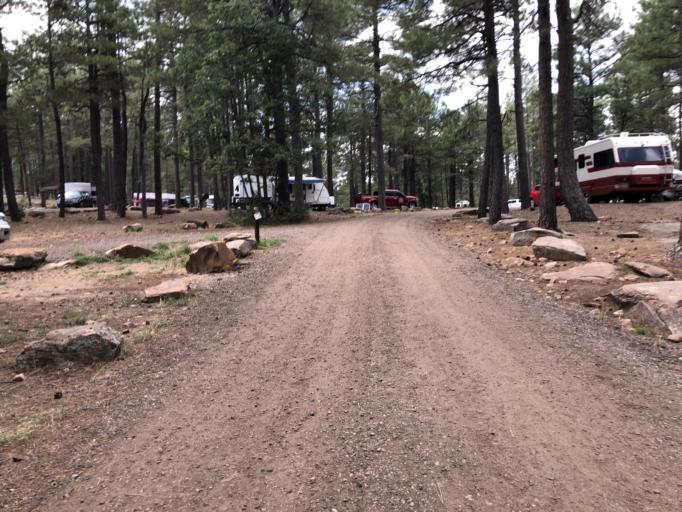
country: US
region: Arizona
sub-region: Gila County
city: Star Valley
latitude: 34.3328
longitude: -110.9373
